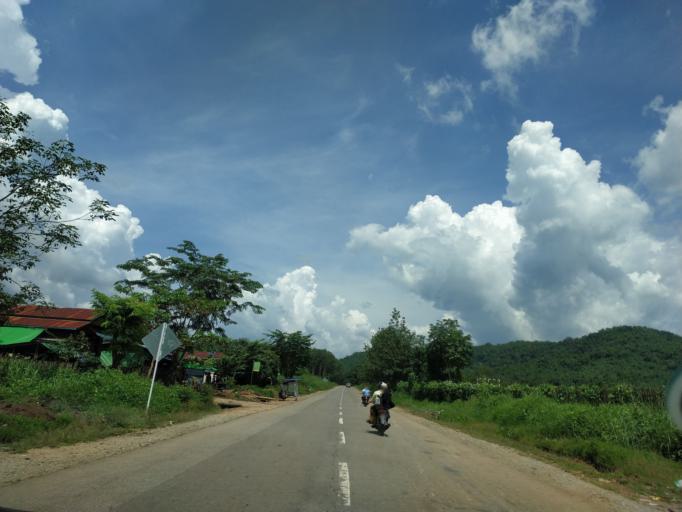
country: TH
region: Kanchanaburi
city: Sangkhla Buri
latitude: 15.3796
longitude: 97.8891
